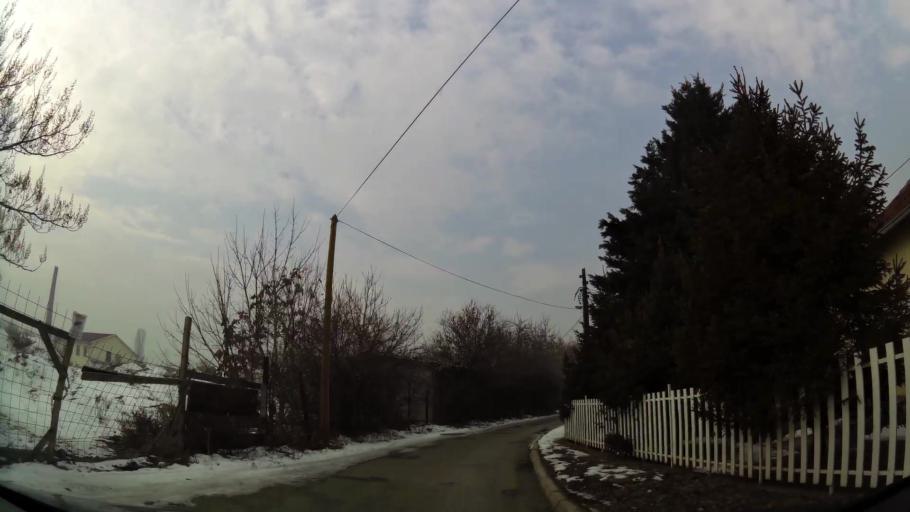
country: MK
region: Cair
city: Cair
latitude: 41.9947
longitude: 21.4604
